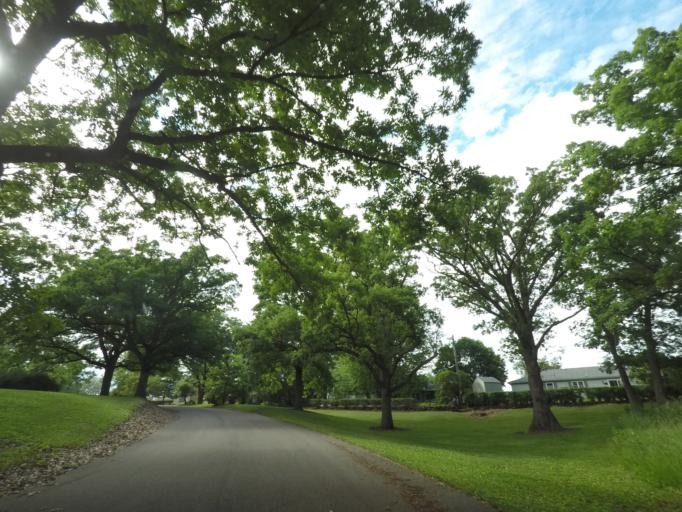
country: US
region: Wisconsin
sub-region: Rock County
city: Janesville
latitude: 42.6795
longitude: -88.9941
